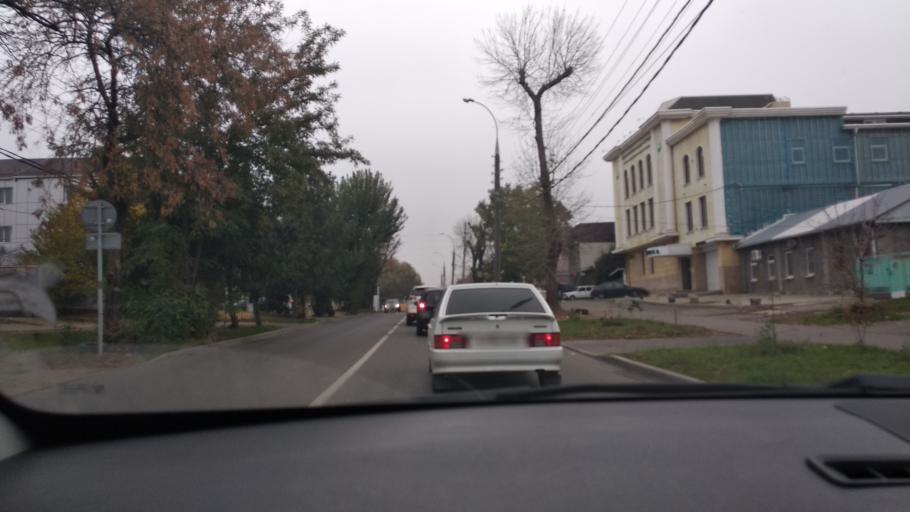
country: RU
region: Krasnodarskiy
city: Krasnodar
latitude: 45.0226
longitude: 39.0096
